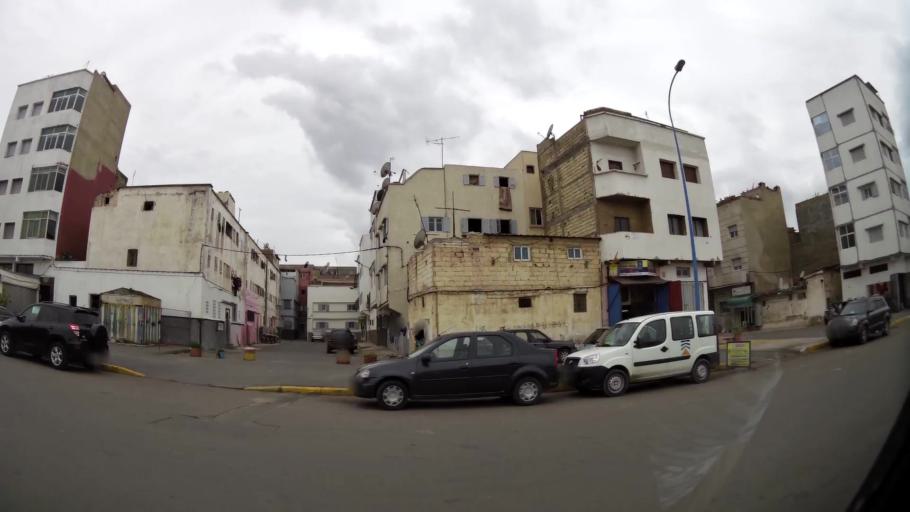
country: MA
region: Grand Casablanca
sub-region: Casablanca
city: Casablanca
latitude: 33.5676
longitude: -7.5656
